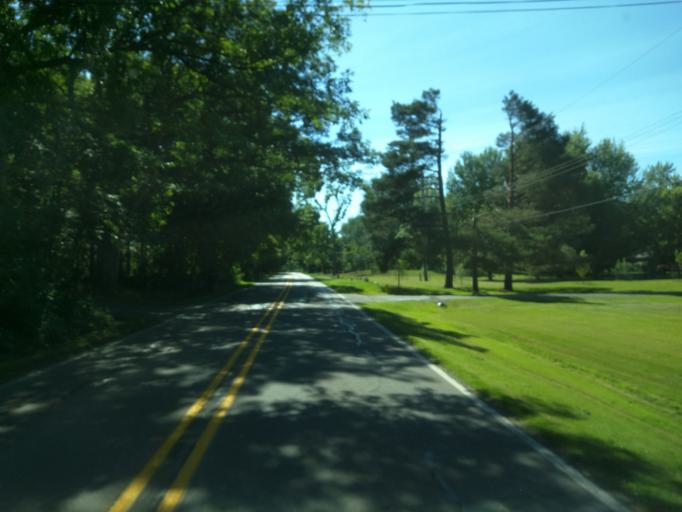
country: US
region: Michigan
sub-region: Eaton County
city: Waverly
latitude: 42.7656
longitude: -84.6230
